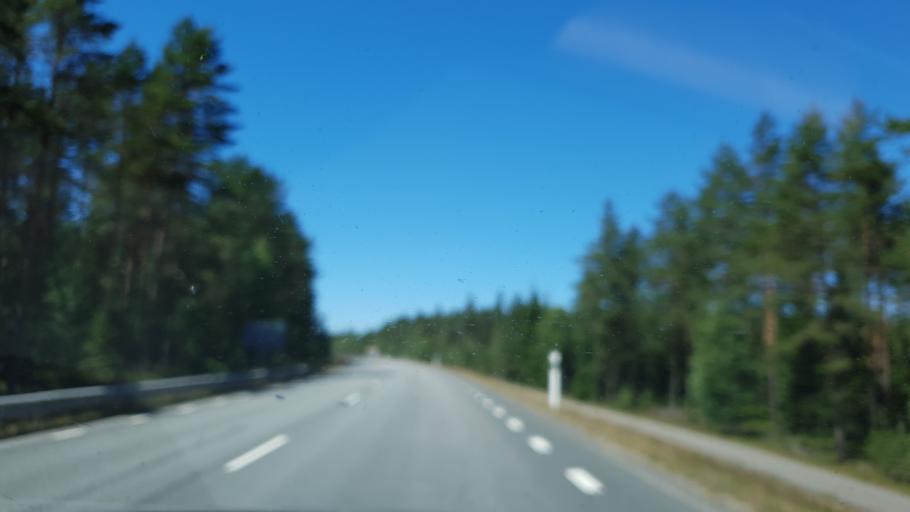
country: SE
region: Joenkoeping
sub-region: Vaggeryds Kommun
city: Vaggeryd
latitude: 57.5242
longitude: 14.1330
